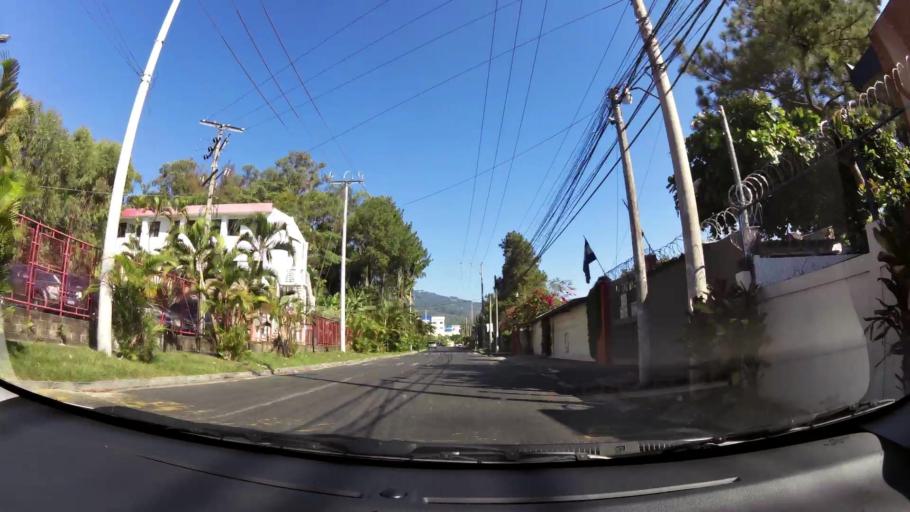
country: SV
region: La Libertad
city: Santa Tecla
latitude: 13.6746
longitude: -89.2762
